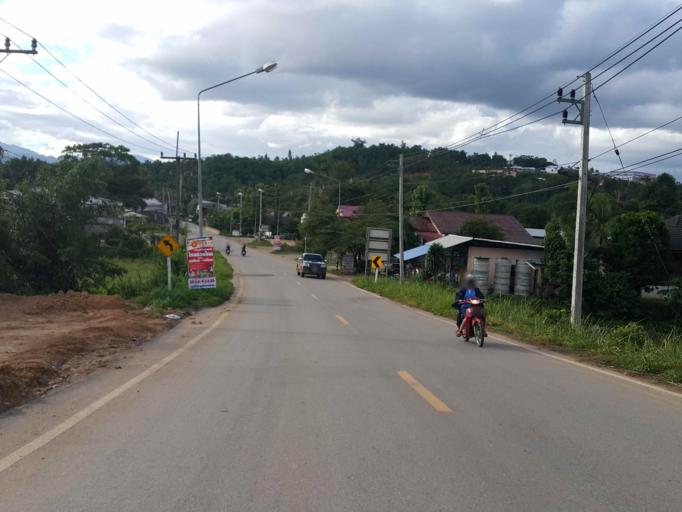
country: TH
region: Chiang Mai
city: Mae Chaem
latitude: 18.4897
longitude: 98.3776
